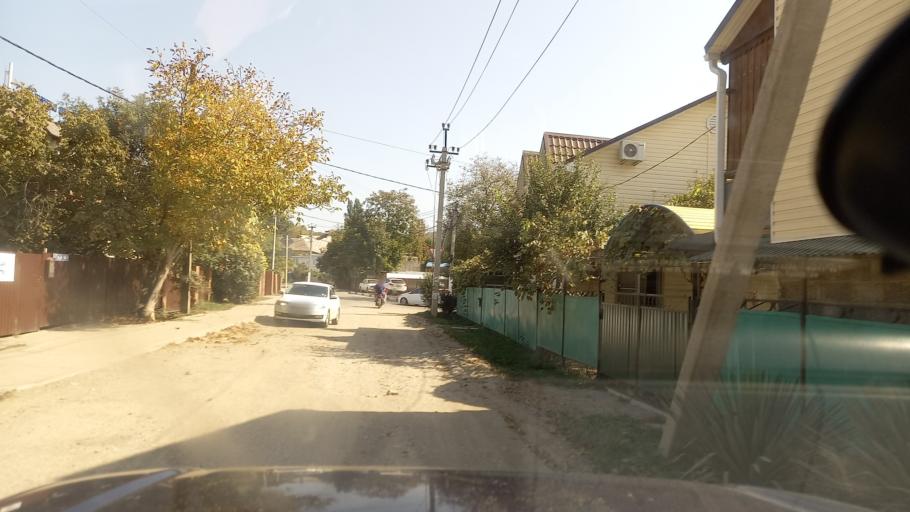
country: RU
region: Krasnodarskiy
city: Arkhipo-Osipovka
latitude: 44.3650
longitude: 38.5280
